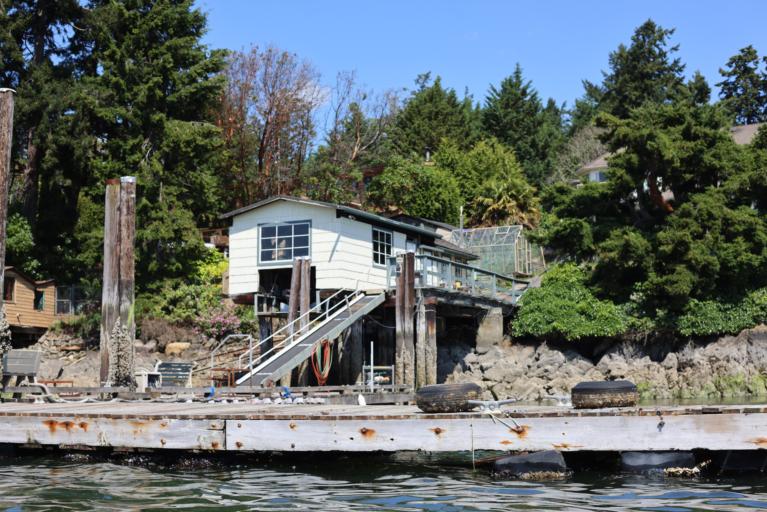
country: CA
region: British Columbia
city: Colwood
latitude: 48.4489
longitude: -123.4358
